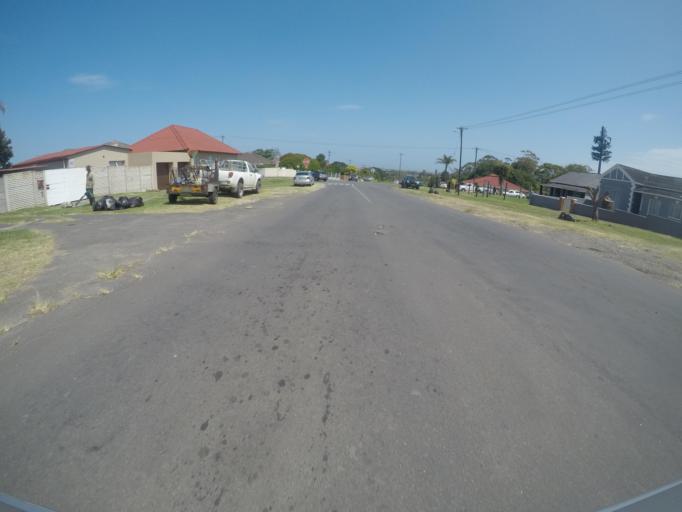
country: ZA
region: Eastern Cape
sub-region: Buffalo City Metropolitan Municipality
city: East London
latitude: -32.9804
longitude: 27.8856
